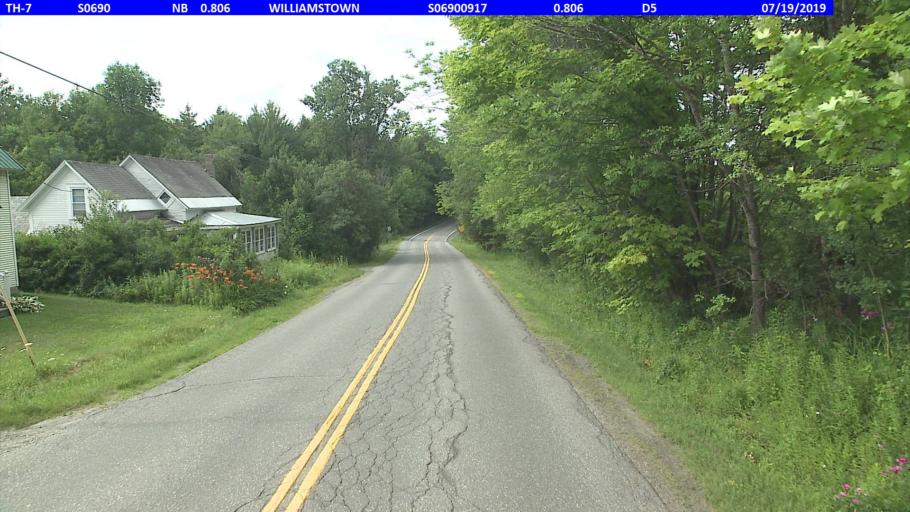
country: US
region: Vermont
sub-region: Washington County
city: South Barre
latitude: 44.1431
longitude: -72.4921
